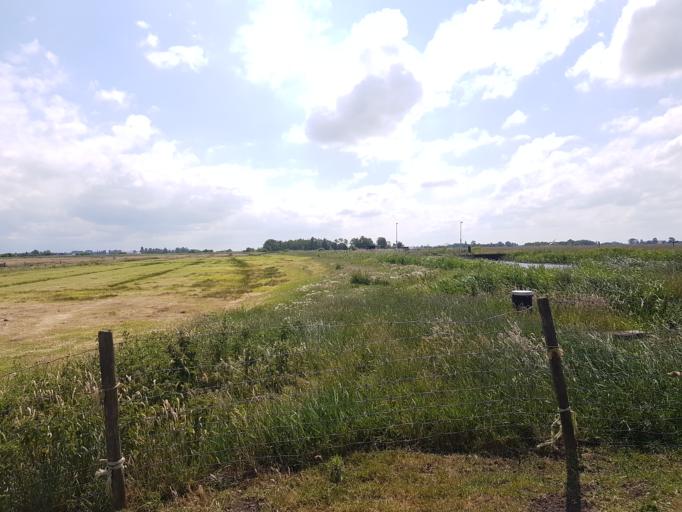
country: NL
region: Friesland
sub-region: Gemeente Boarnsterhim
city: Aldeboarn
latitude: 53.0940
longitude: 5.9015
